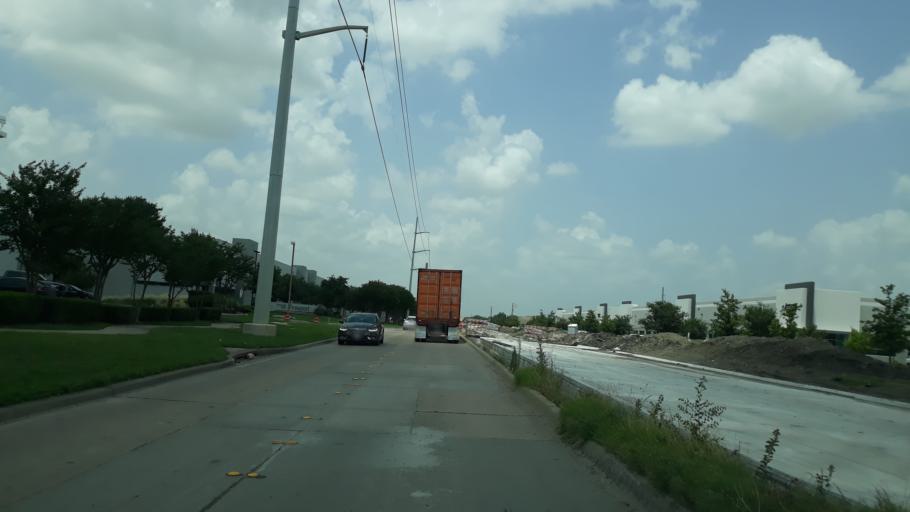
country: US
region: Texas
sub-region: Dallas County
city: Coppell
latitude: 32.9452
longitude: -97.0111
